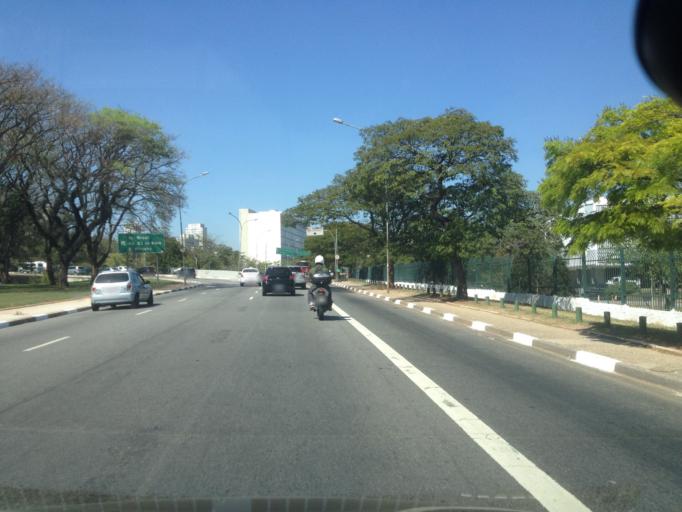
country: BR
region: Sao Paulo
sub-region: Sao Paulo
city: Sao Paulo
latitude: -23.5865
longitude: -46.6543
